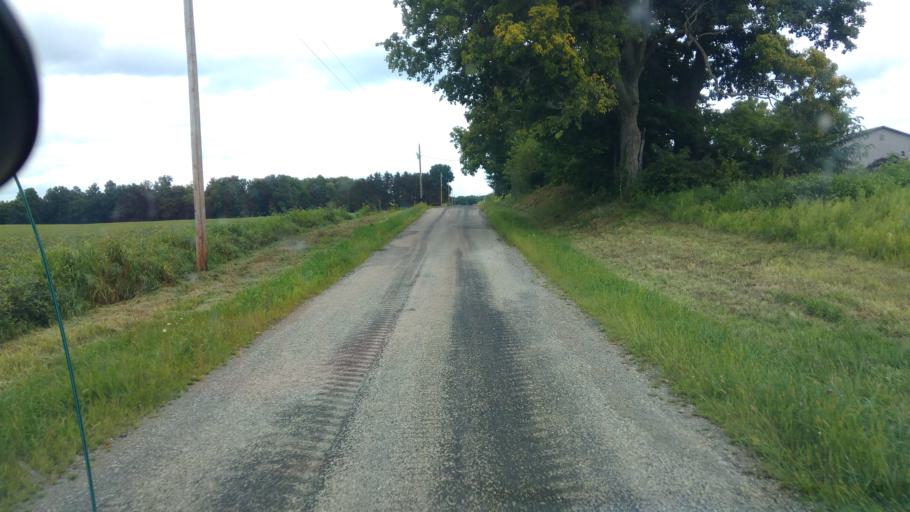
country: US
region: Ohio
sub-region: Richland County
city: Lincoln Heights
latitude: 40.8331
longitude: -82.4131
